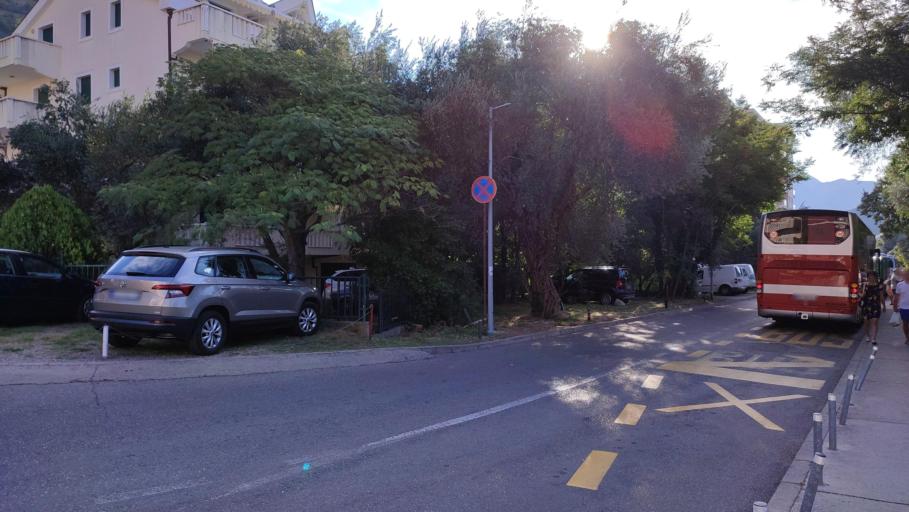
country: ME
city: Petrovac na Moru
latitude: 42.2077
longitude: 18.9407
